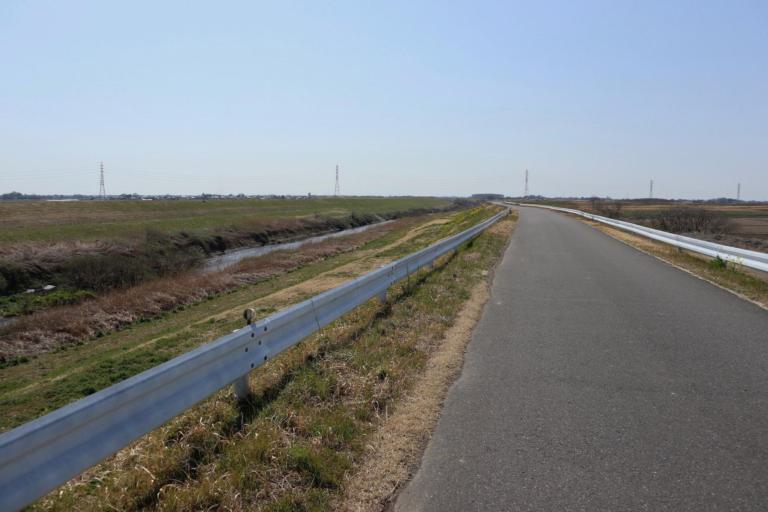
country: JP
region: Tochigi
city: Fujioka
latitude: 36.2715
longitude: 139.7068
